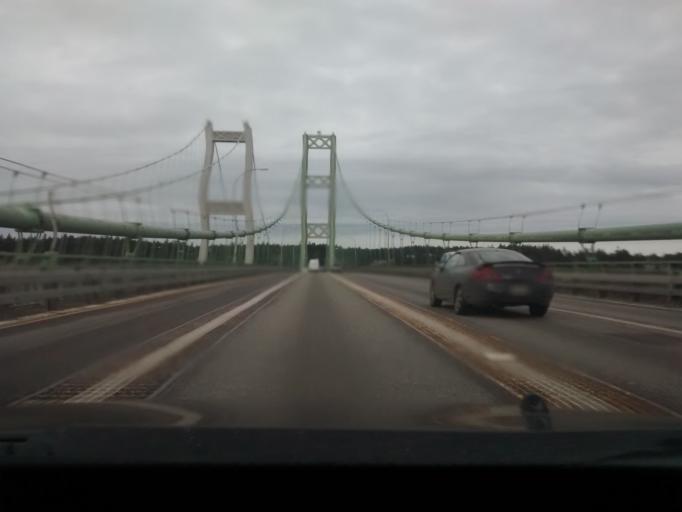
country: US
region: Washington
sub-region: Pierce County
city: University Place
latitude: 47.2684
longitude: -122.5504
